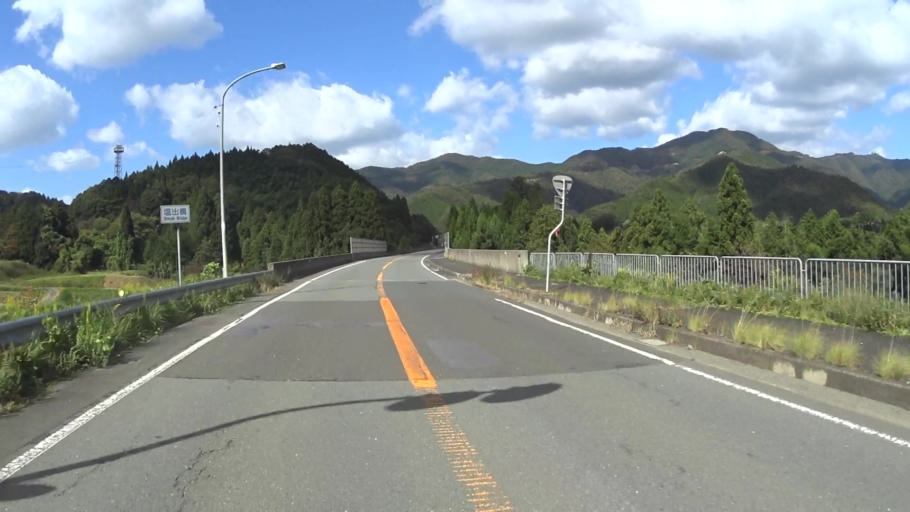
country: JP
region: Kyoto
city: Ayabe
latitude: 35.2682
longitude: 135.3655
